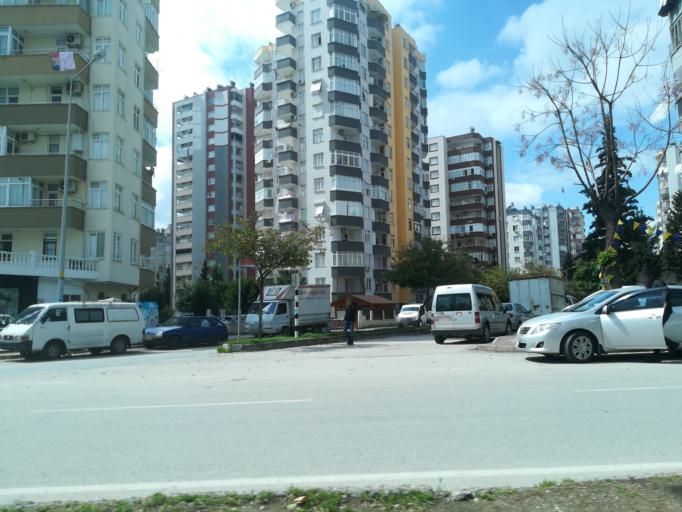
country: TR
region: Adana
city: Adana
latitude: 37.0410
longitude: 35.3020
